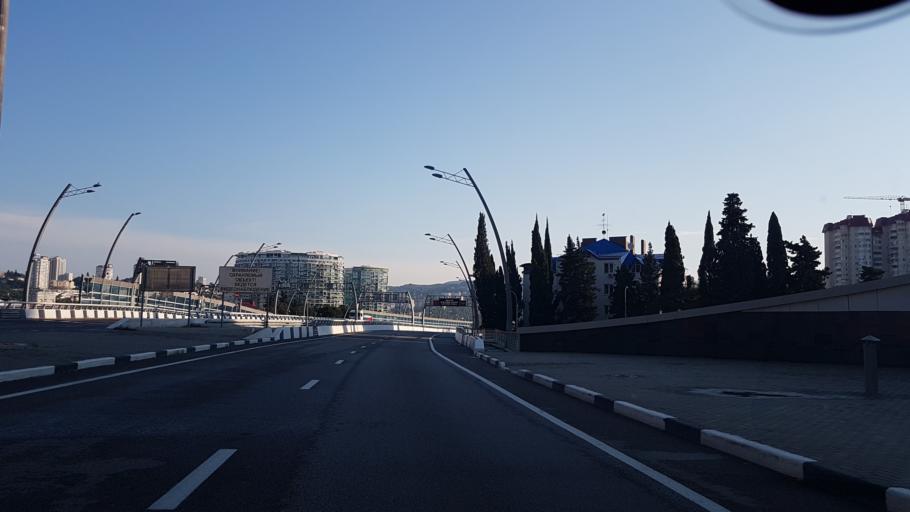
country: RU
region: Krasnodarskiy
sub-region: Sochi City
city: Sochi
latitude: 43.5900
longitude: 39.7304
